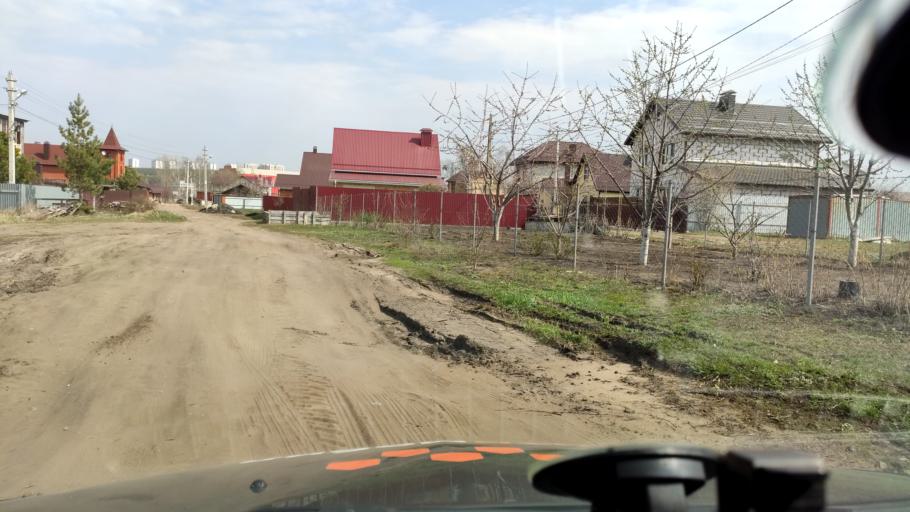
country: RU
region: Voronezj
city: Pridonskoy
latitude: 51.6357
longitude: 39.0997
